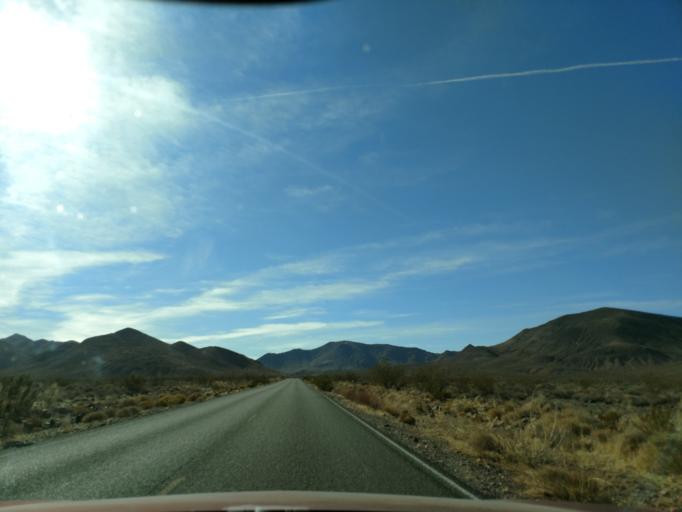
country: US
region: Nevada
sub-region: Nye County
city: Beatty
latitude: 36.8167
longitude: -116.9002
